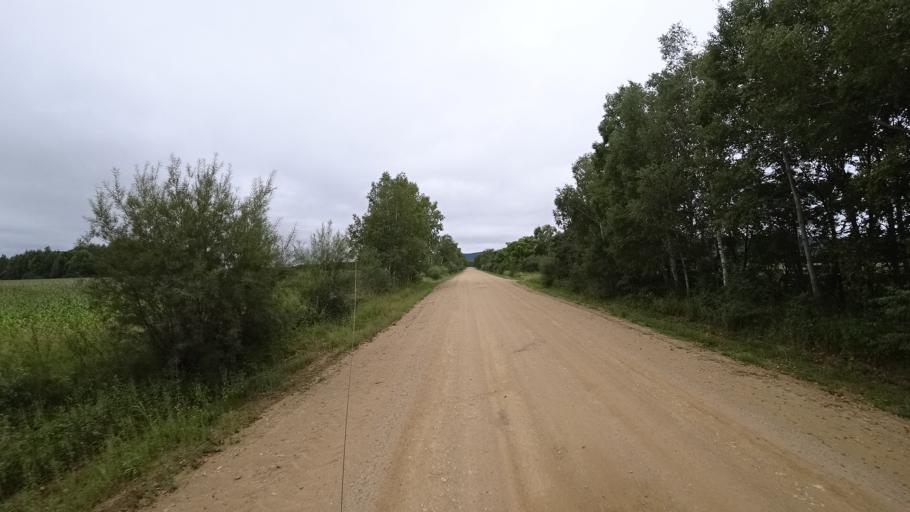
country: RU
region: Primorskiy
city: Rettikhovka
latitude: 44.1596
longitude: 132.6962
